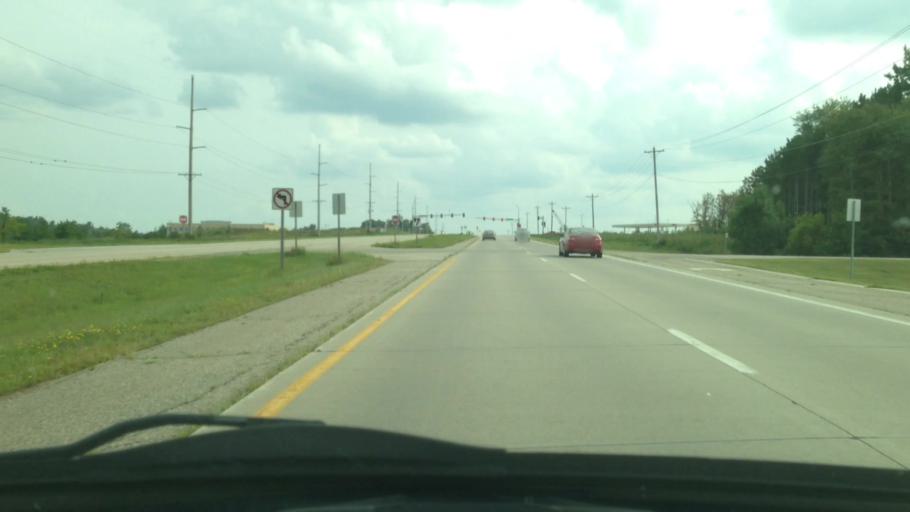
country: US
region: Minnesota
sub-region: Olmsted County
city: Rochester
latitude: 44.0720
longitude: -92.5237
